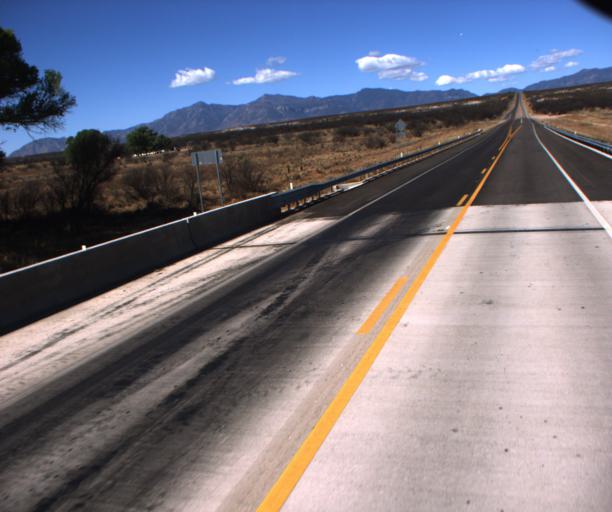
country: US
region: Arizona
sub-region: Cochise County
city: Sierra Vista Southeast
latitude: 31.5518
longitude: -110.1389
